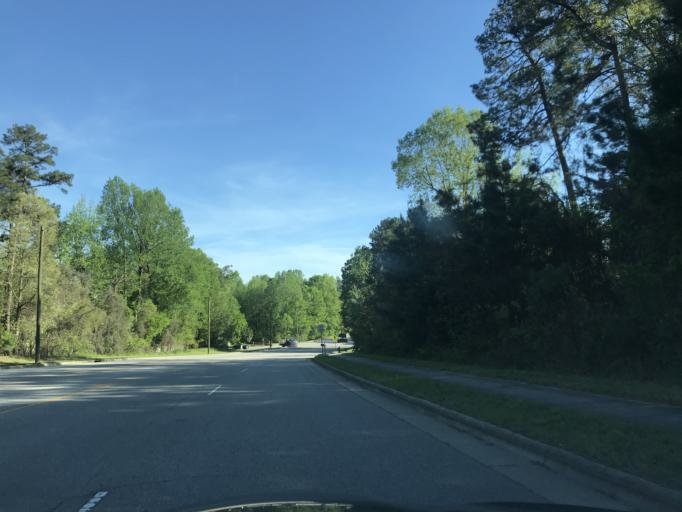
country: US
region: North Carolina
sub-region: Wake County
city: Knightdale
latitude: 35.8119
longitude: -78.5560
